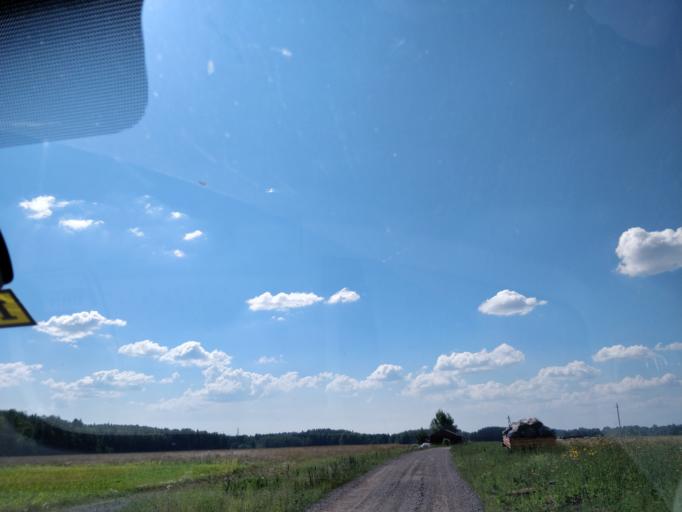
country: FI
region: Uusimaa
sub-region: Helsinki
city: Vantaa
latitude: 60.3107
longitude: 25.0850
